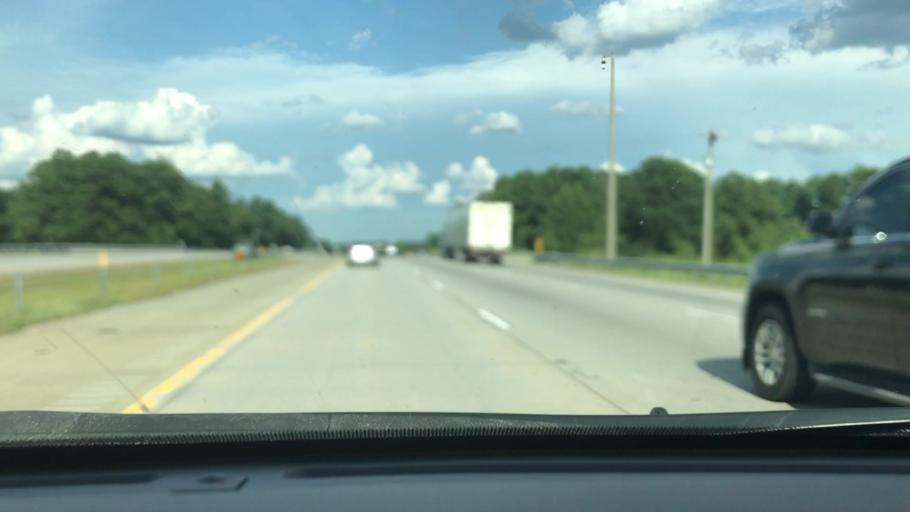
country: US
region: South Carolina
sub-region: Florence County
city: Florence
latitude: 34.2648
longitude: -79.7329
